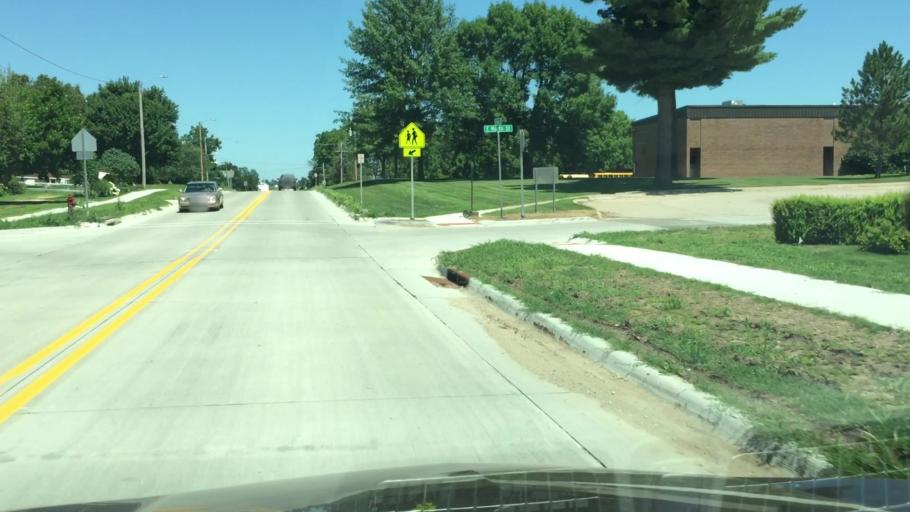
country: US
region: Iowa
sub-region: Cedar County
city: Mechanicsville
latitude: 41.8942
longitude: -91.1520
